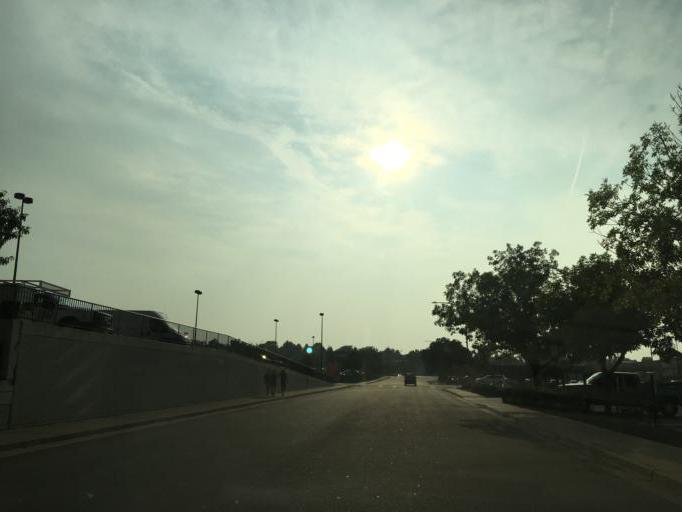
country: US
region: Colorado
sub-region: Arapahoe County
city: Glendale
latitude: 39.7020
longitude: -104.9374
